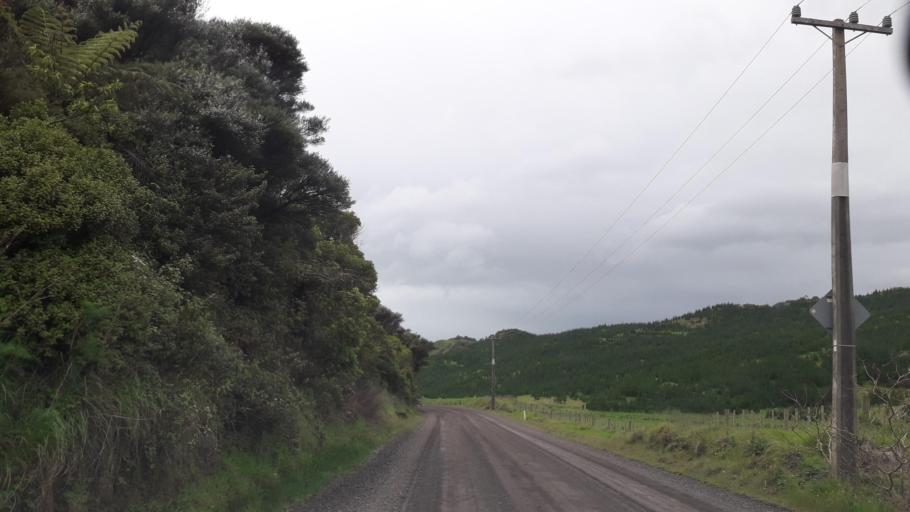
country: NZ
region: Northland
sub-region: Far North District
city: Ahipara
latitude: -35.4307
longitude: 173.3497
